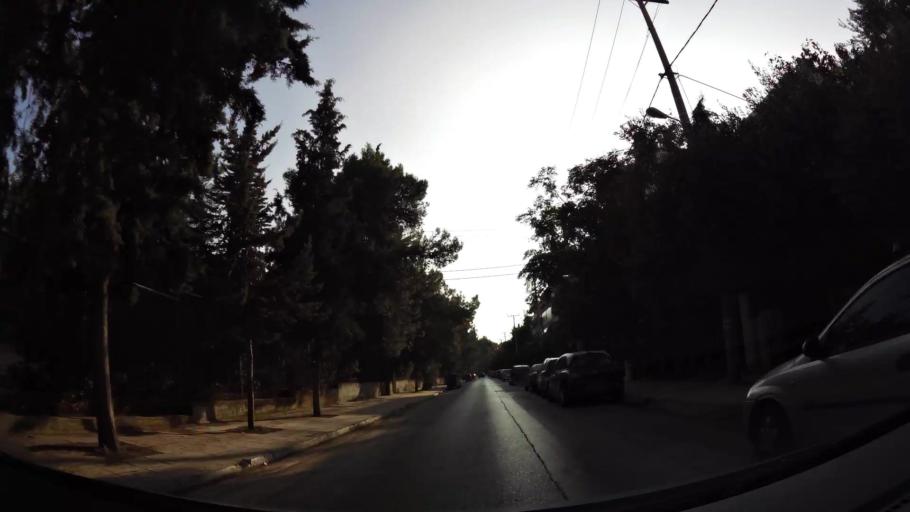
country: GR
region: Attica
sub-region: Nomarchia Athinas
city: Agia Paraskevi
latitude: 38.0024
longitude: 23.8231
